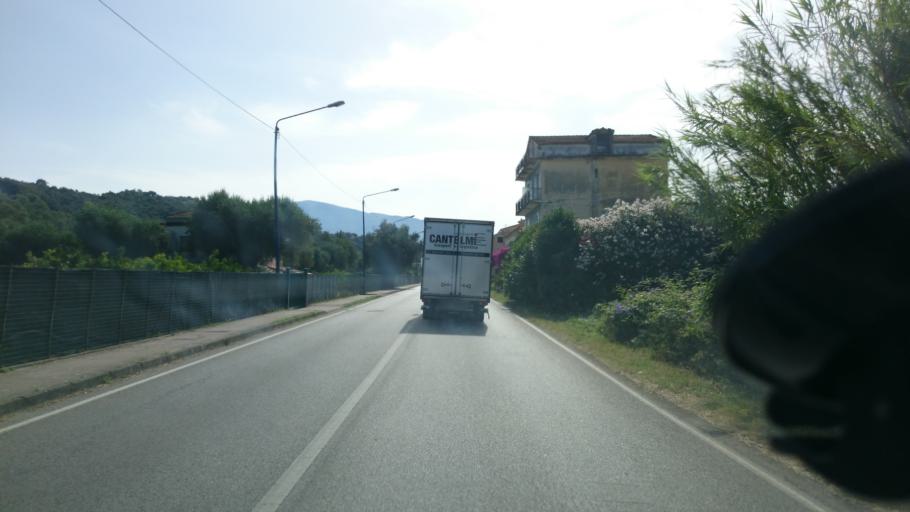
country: IT
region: Campania
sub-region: Provincia di Salerno
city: Ispani
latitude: 40.0763
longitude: 15.5483
